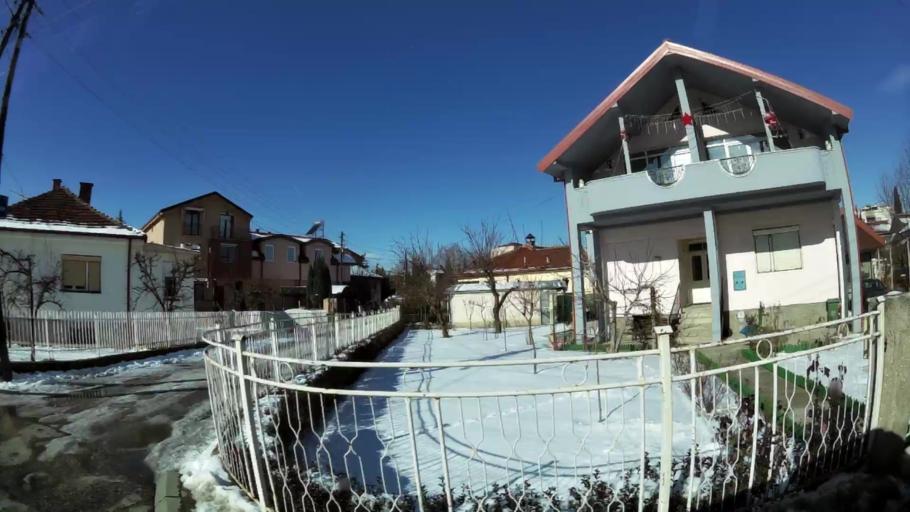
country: MK
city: Krushopek
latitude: 42.0032
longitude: 21.3541
